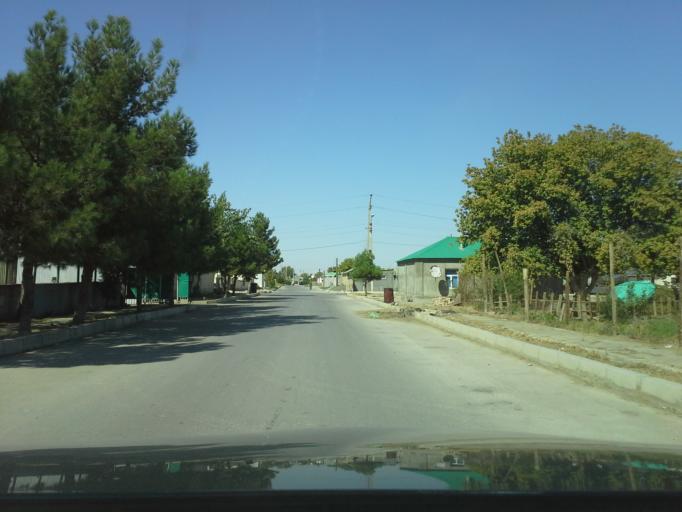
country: TM
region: Ahal
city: Abadan
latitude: 38.0184
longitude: 58.2715
